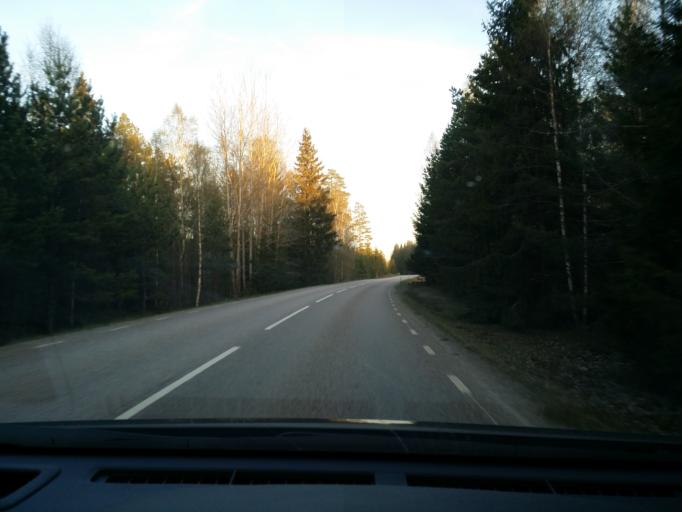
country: SE
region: Vaestmanland
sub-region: Sala Kommun
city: Sala
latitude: 59.8115
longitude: 16.5435
